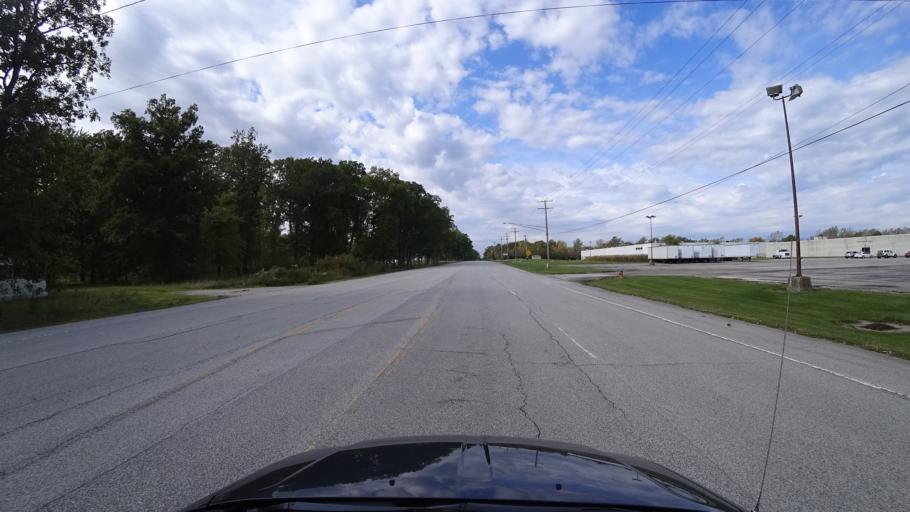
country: US
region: Indiana
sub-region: LaPorte County
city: Michigan City
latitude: 41.6659
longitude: -86.9049
